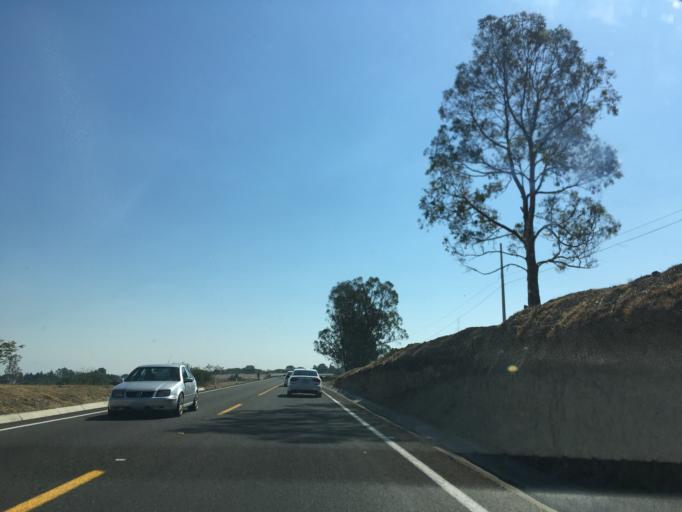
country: MX
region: Michoacan
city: Charo
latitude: 19.7612
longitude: -101.0321
